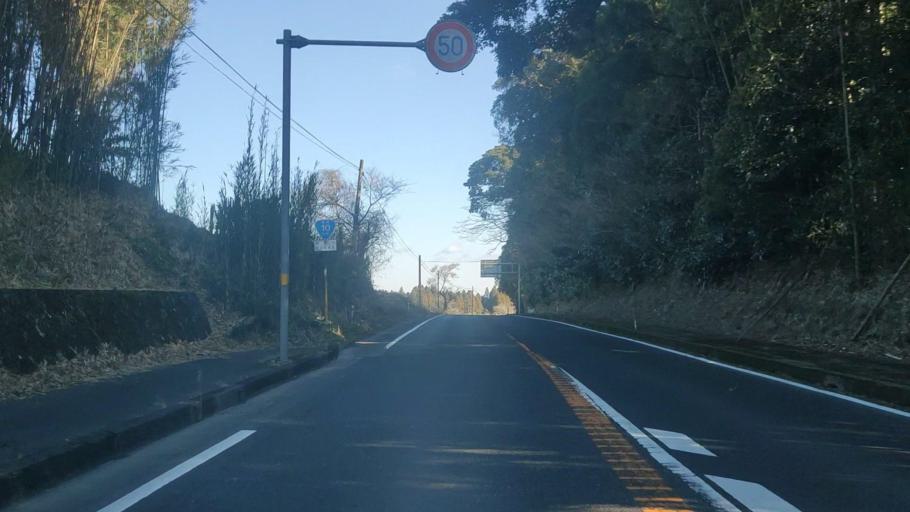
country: JP
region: Kagoshima
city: Sueyoshicho-ninokata
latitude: 31.6685
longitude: 130.9123
